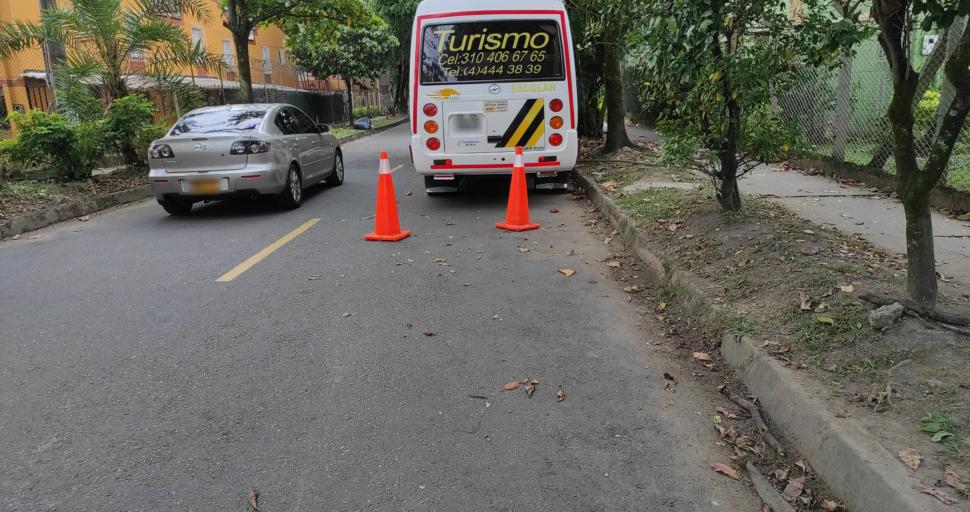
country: CO
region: Antioquia
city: Itagui
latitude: 6.1934
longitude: -75.5950
